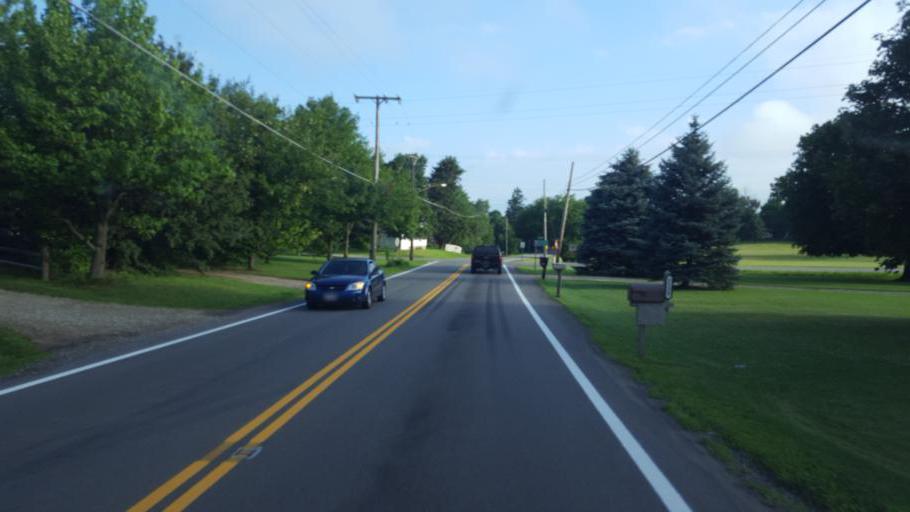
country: US
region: Ohio
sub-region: Richland County
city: Ontario
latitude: 40.7830
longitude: -82.6536
